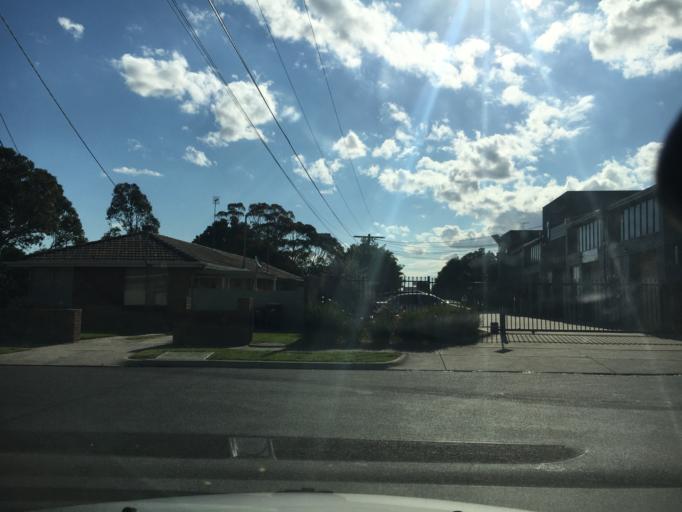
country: AU
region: Victoria
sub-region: Greater Dandenong
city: Springvale
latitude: -37.9342
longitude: 145.1497
